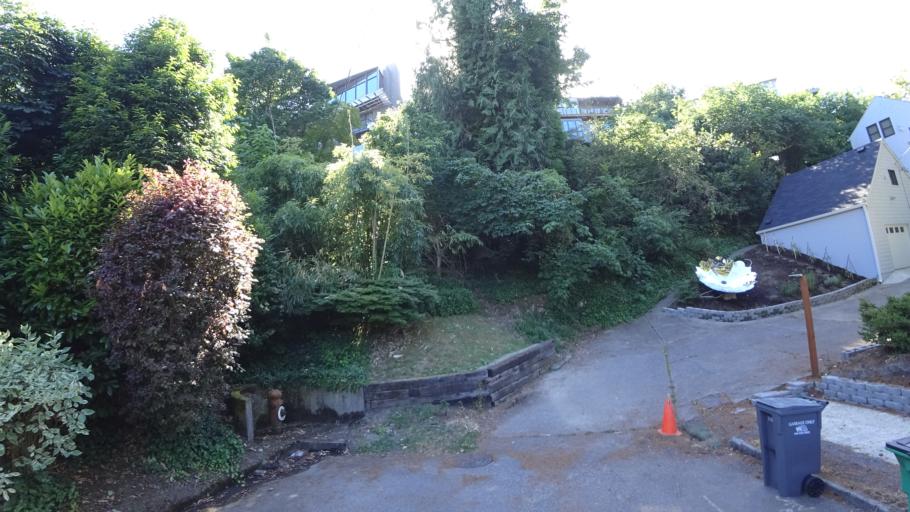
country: US
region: Oregon
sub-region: Multnomah County
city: Portland
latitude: 45.5309
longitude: -122.7110
